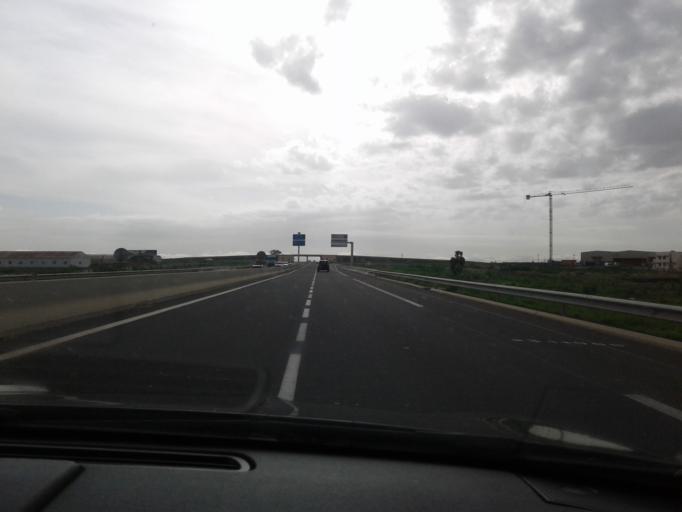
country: SN
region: Thies
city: Thies
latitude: 14.7322
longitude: -17.2126
